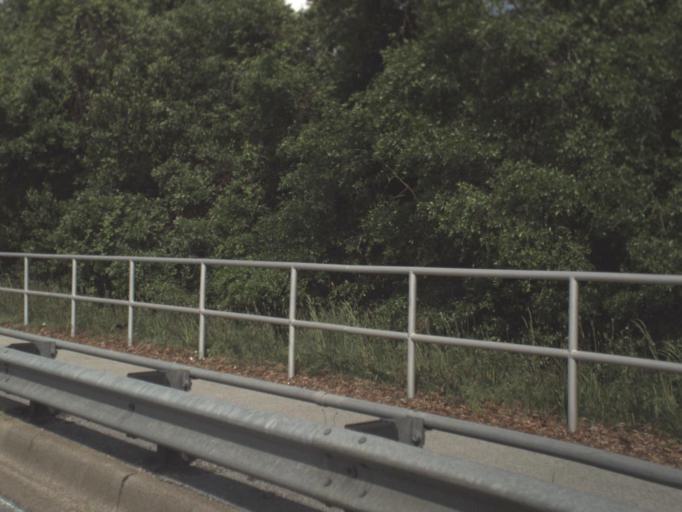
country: US
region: Florida
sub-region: Escambia County
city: Ferry Pass
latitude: 30.5008
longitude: -87.1843
